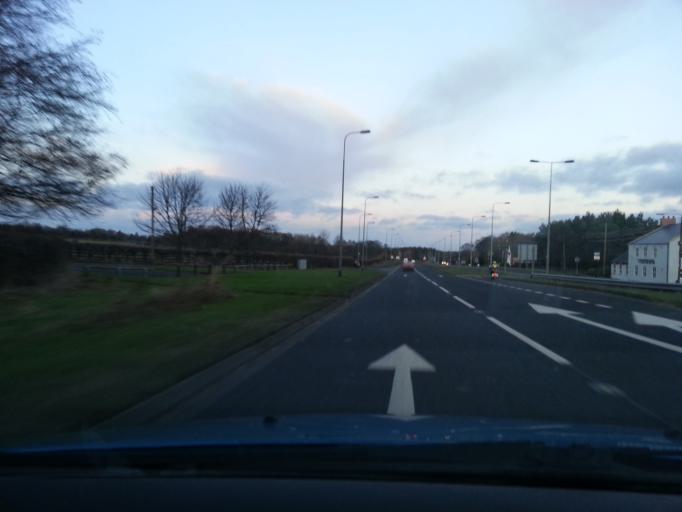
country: GB
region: England
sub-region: County Durham
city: Chester-le-Street
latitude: 54.8366
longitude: -1.5882
